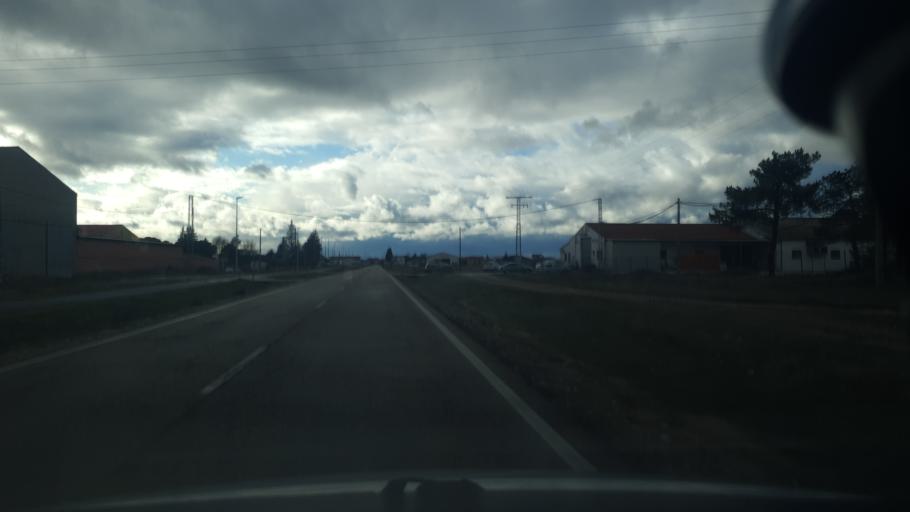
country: ES
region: Castille and Leon
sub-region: Provincia de Segovia
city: Sanchonuno
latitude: 41.2916
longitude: -4.3134
